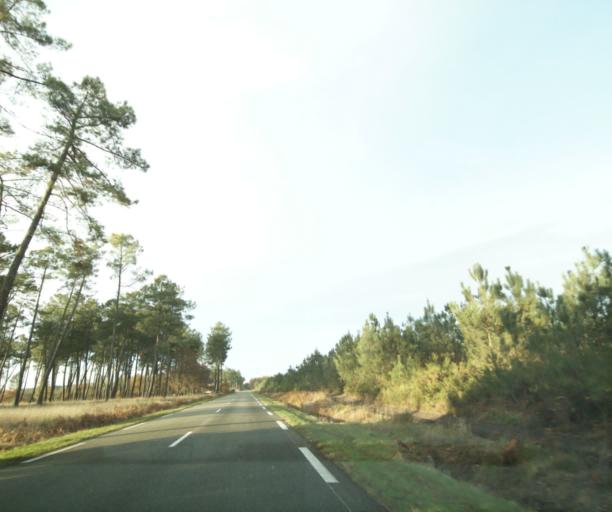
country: FR
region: Aquitaine
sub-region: Departement des Landes
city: Gabarret
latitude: 44.0280
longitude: -0.0277
